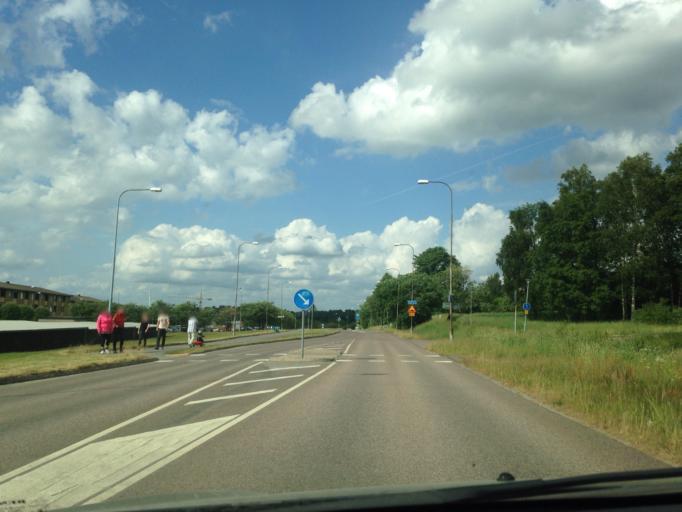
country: SE
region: Vaestra Goetaland
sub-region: Goteborg
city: Majorna
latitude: 57.7468
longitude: 11.9265
